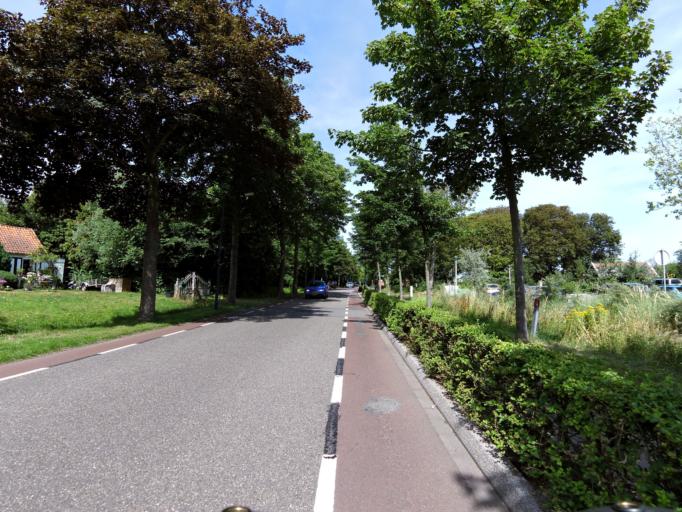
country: NL
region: Zeeland
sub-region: Schouwen-Duiveland
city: Burgh
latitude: 51.6843
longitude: 3.7225
